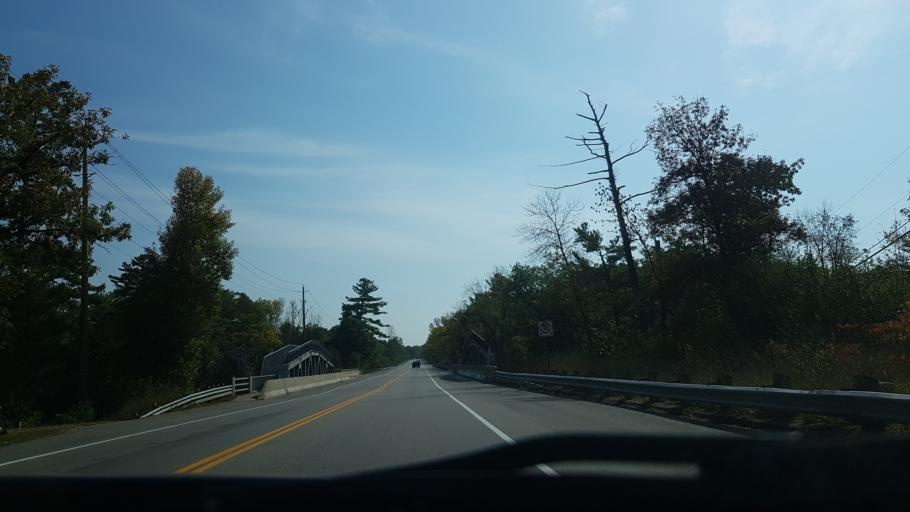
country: CA
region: Ontario
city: Orillia
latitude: 44.7468
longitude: -79.3256
